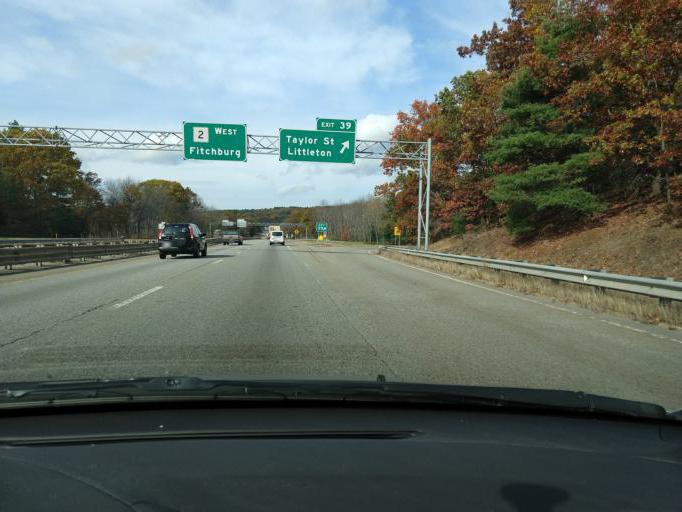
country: US
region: Massachusetts
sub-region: Middlesex County
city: Littleton Common
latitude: 42.5233
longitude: -71.5135
